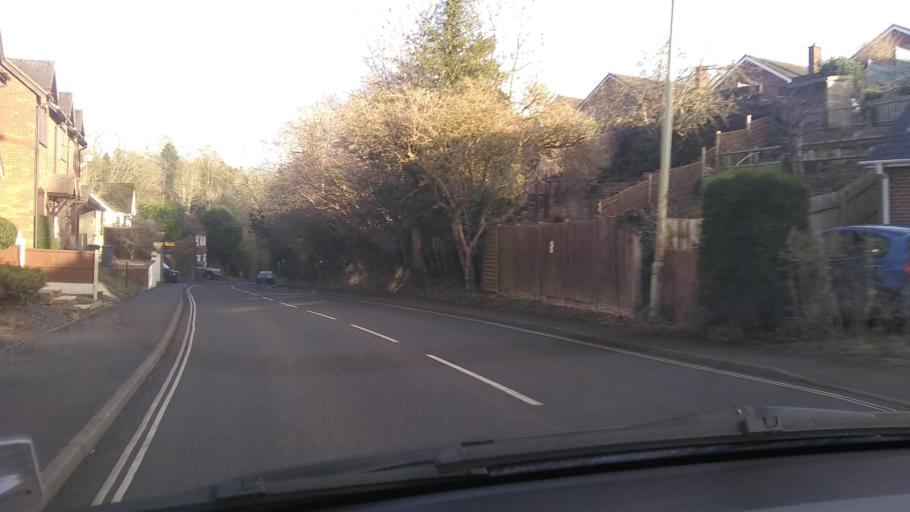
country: GB
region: England
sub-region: Worcestershire
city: Bewdley
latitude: 52.3750
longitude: -2.3255
